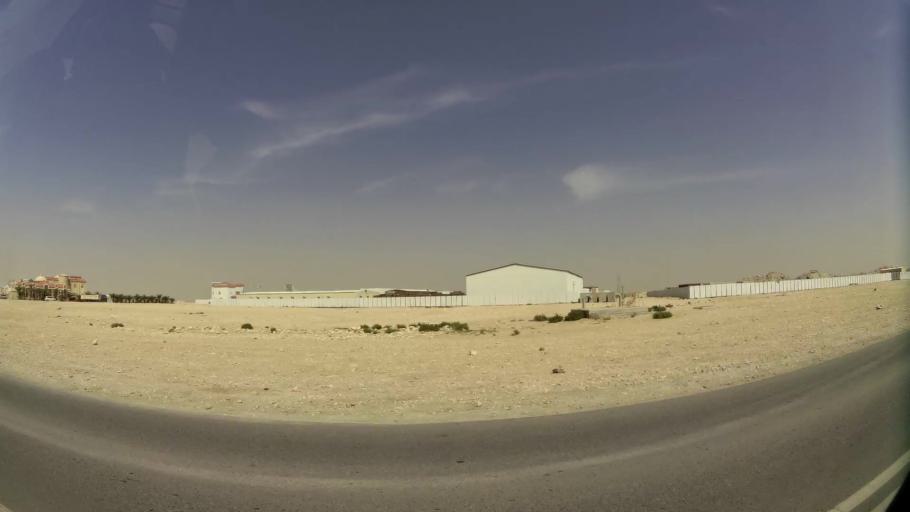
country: QA
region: Baladiyat ar Rayyan
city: Ar Rayyan
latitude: 25.2627
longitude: 51.3808
